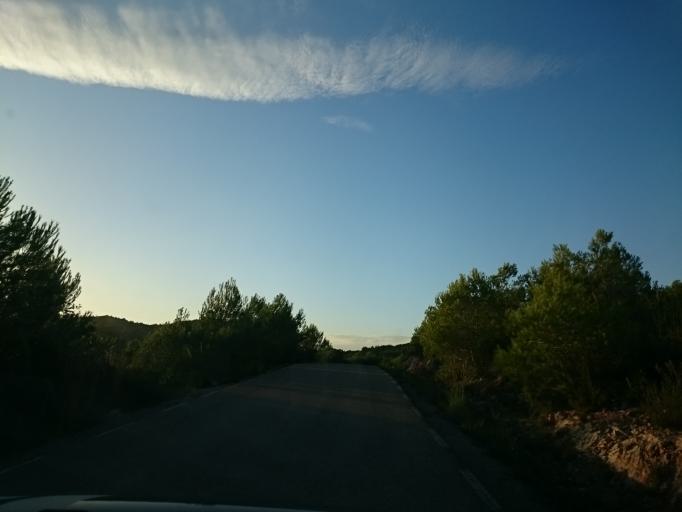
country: ES
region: Catalonia
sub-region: Provincia de Barcelona
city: Olivella
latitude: 41.3039
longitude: 1.8235
